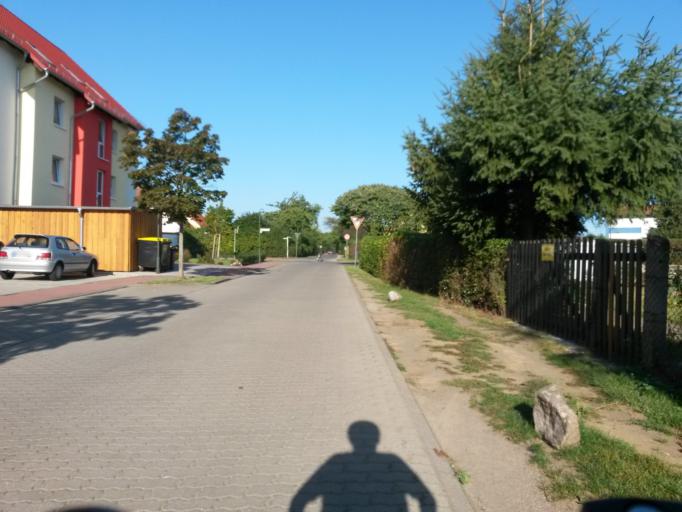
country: DE
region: Brandenburg
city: Templin
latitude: 53.1242
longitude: 13.4867
